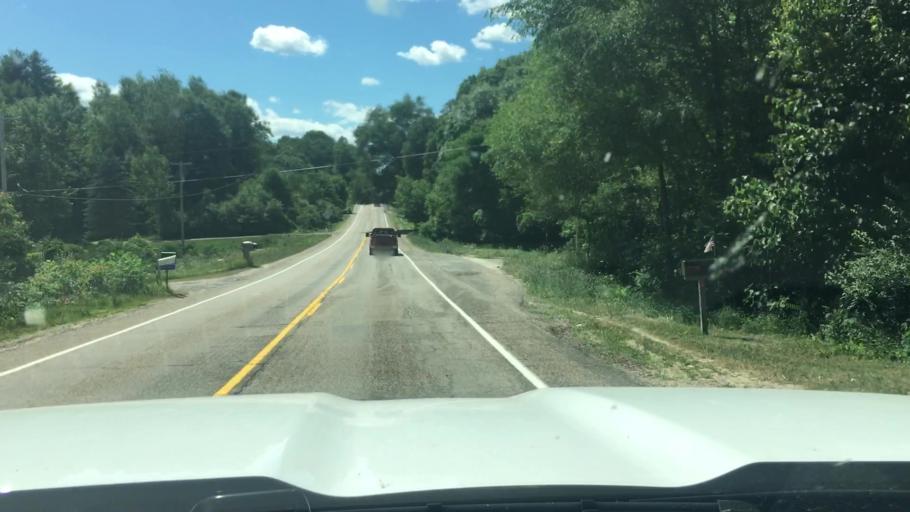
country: US
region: Michigan
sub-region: Kent County
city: Cedar Springs
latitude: 43.1756
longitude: -85.5855
